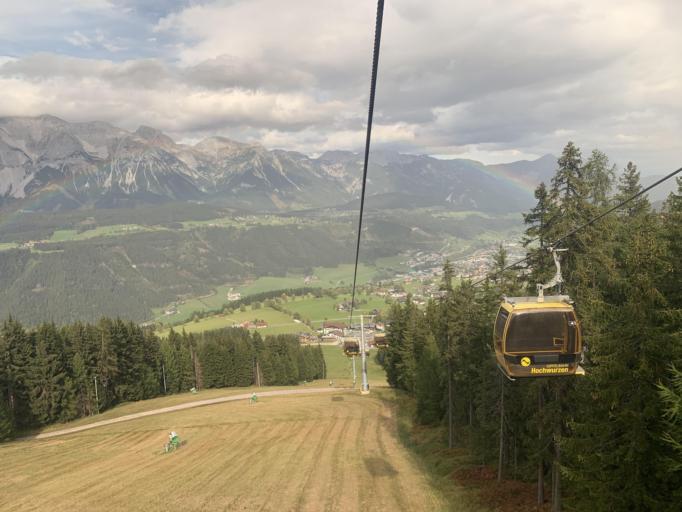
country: AT
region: Styria
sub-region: Politischer Bezirk Liezen
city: Schladming
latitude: 47.3706
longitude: 13.6488
